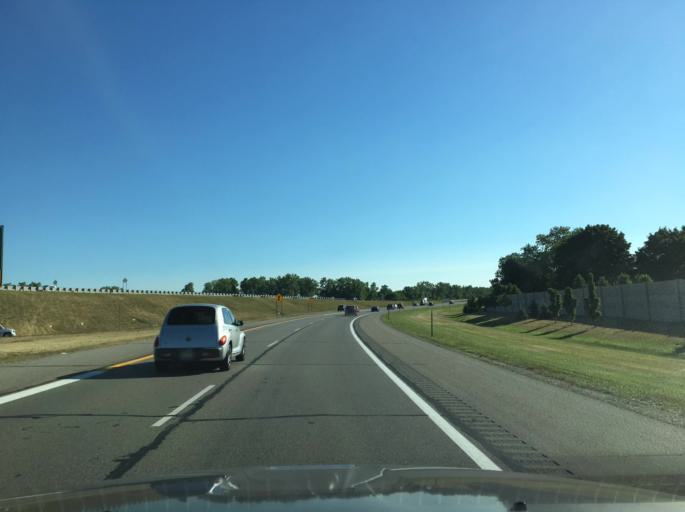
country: US
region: Michigan
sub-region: Macomb County
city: Sterling Heights
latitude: 42.5985
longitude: -83.0289
